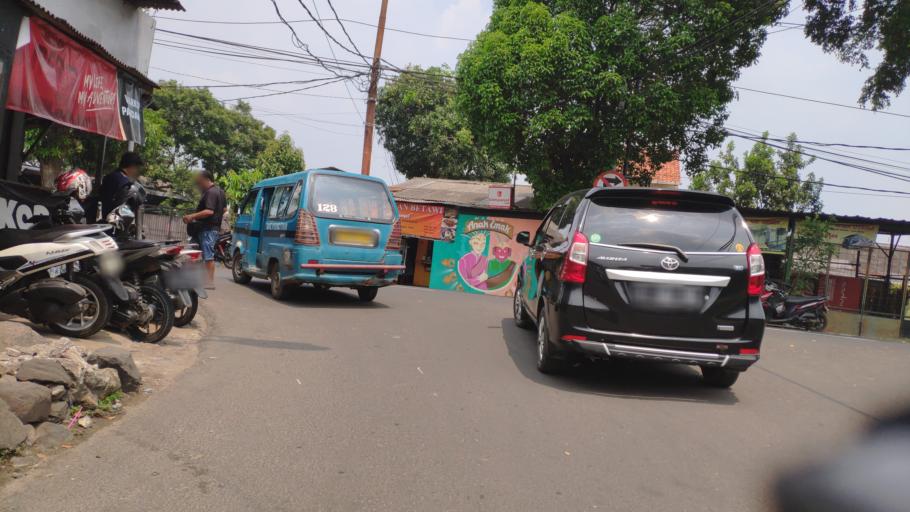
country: ID
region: West Java
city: Depok
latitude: -6.3451
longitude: 106.8323
